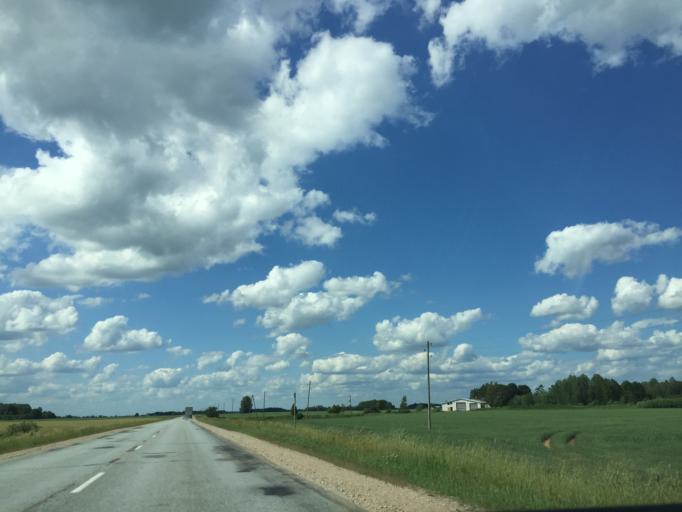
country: LV
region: Engure
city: Smarde
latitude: 56.8872
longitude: 23.2540
